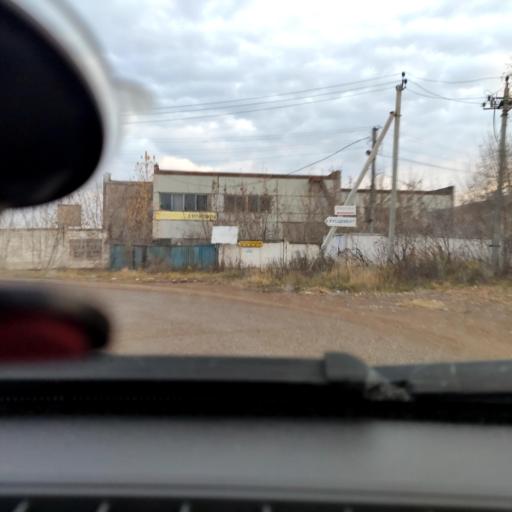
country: RU
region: Bashkortostan
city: Ufa
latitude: 54.7474
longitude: 55.9235
